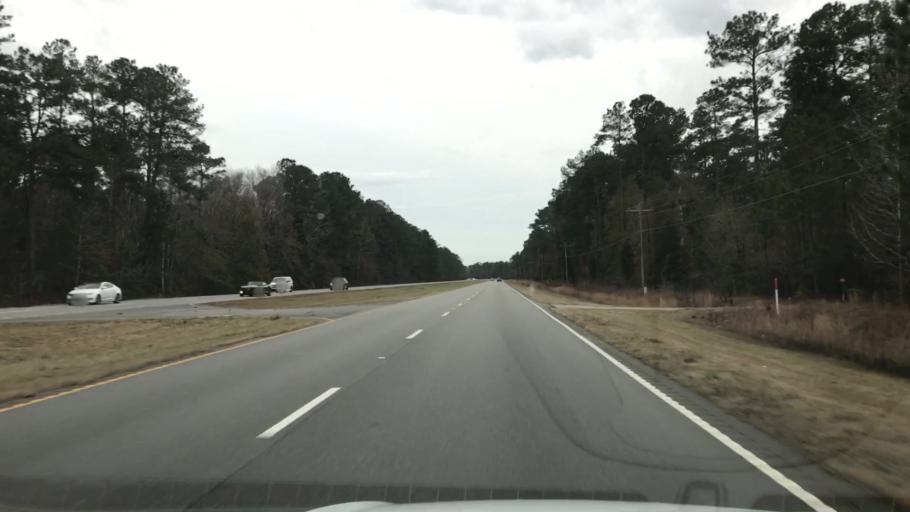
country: US
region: South Carolina
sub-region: Georgetown County
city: Georgetown
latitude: 33.2610
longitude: -79.3662
